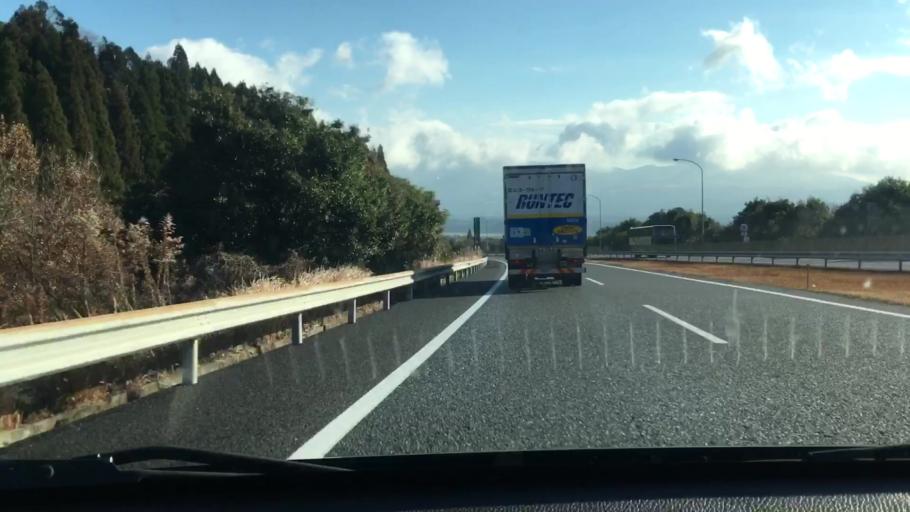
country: JP
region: Kumamoto
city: Hitoyoshi
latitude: 32.0737
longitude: 130.7933
